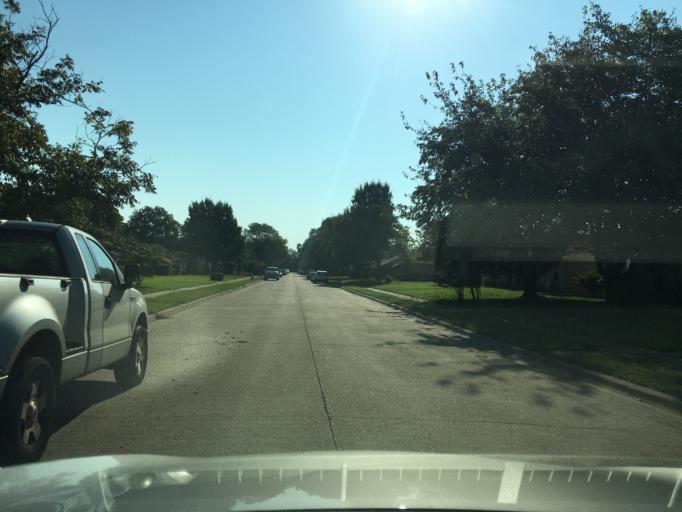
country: US
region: Texas
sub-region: Dallas County
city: Garland
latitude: 32.9501
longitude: -96.6601
